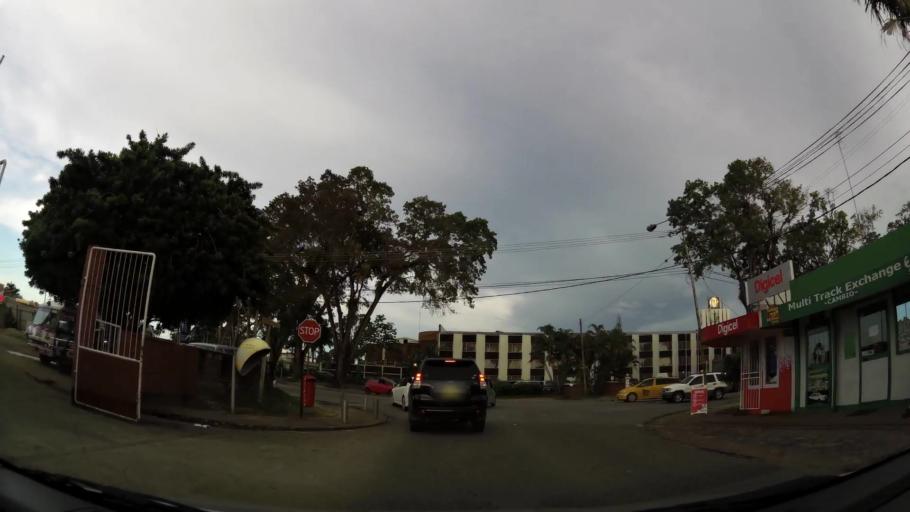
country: SR
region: Paramaribo
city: Paramaribo
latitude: 5.8290
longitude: -55.1469
